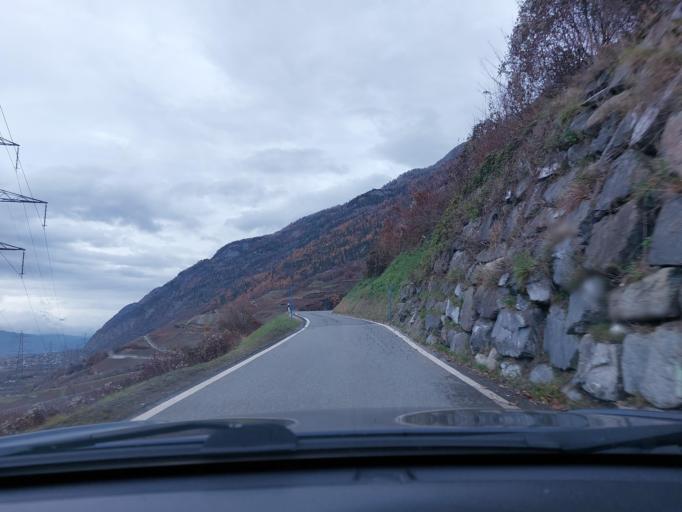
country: CH
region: Valais
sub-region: Martigny District
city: Saxon
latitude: 46.1457
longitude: 7.1870
